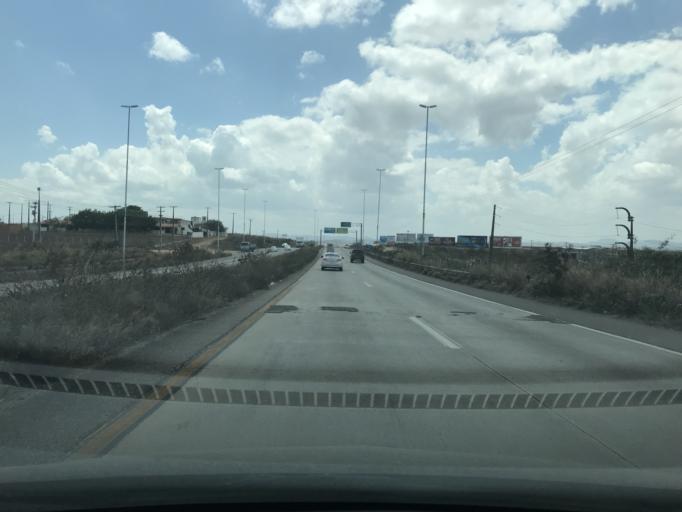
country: BR
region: Pernambuco
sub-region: Caruaru
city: Caruaru
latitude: -8.3015
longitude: -35.9830
